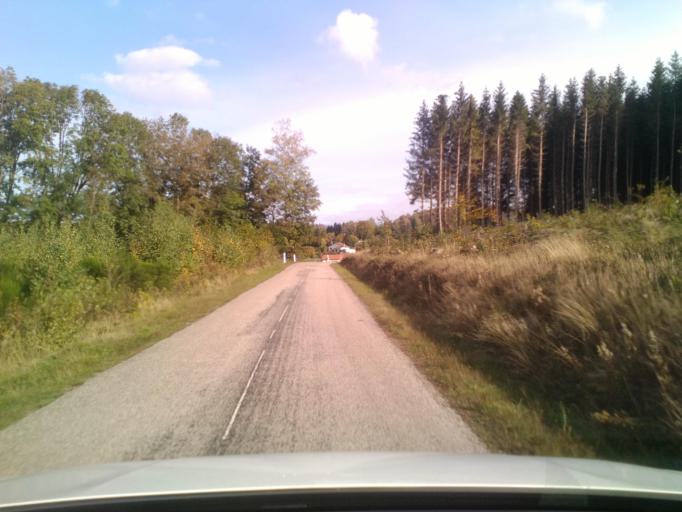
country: FR
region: Lorraine
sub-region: Departement des Vosges
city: Senones
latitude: 48.3837
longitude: 7.0546
